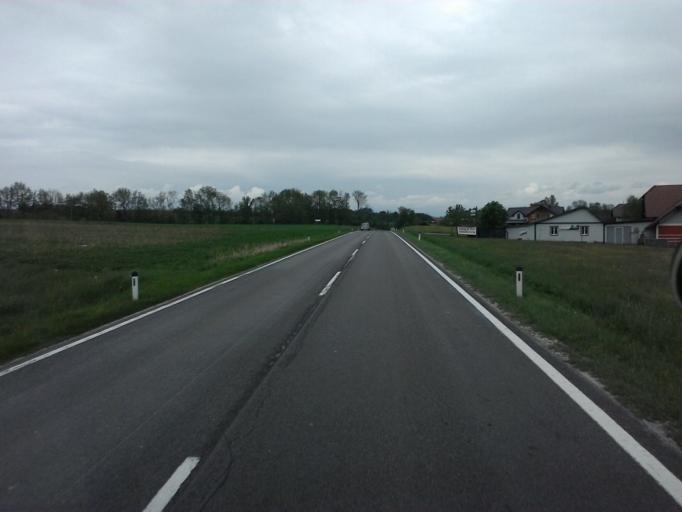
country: AT
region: Upper Austria
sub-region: Politischer Bezirk Vocklabruck
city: Wolfsegg am Hausruck
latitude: 48.2158
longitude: 13.6910
